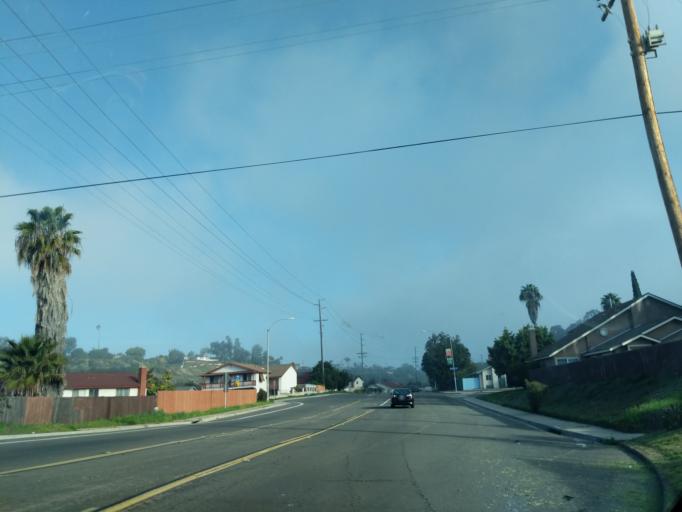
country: US
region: California
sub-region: San Diego County
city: National City
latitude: 32.7295
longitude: -117.0891
